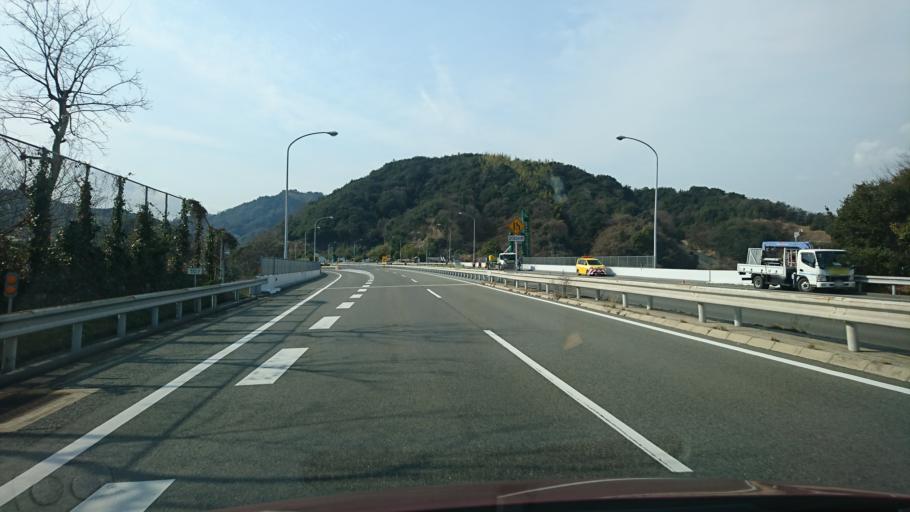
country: JP
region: Hiroshima
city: Onomichi
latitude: 34.3540
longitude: 133.1728
